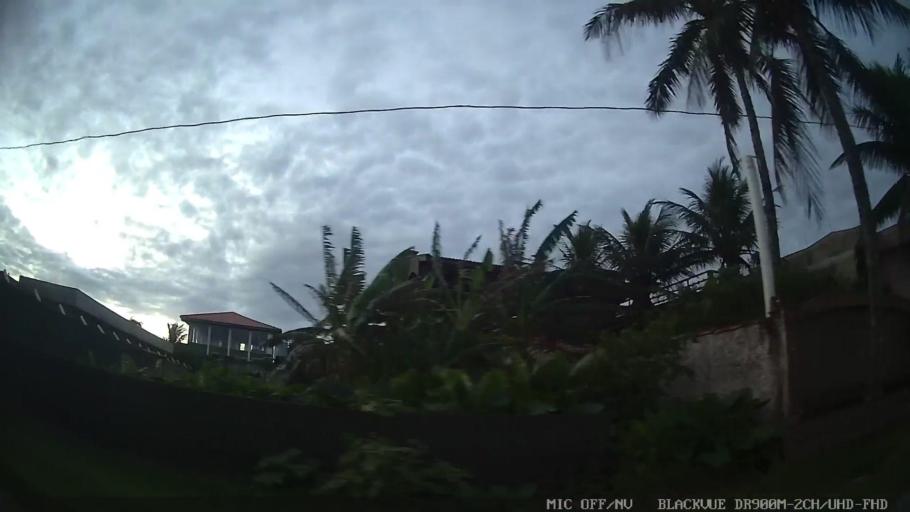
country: BR
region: Sao Paulo
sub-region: Itanhaem
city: Itanhaem
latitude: -24.2421
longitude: -46.8843
